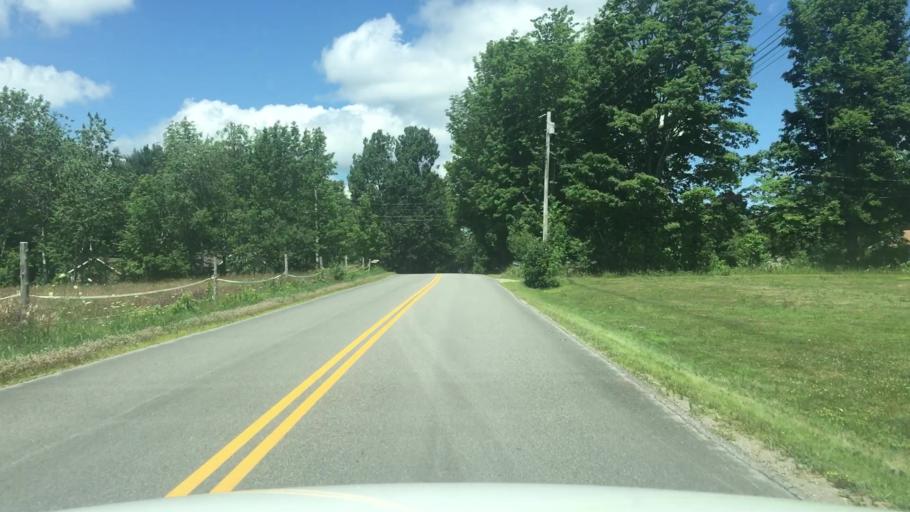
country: US
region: Maine
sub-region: Waldo County
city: Belfast
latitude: 44.4131
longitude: -69.0391
